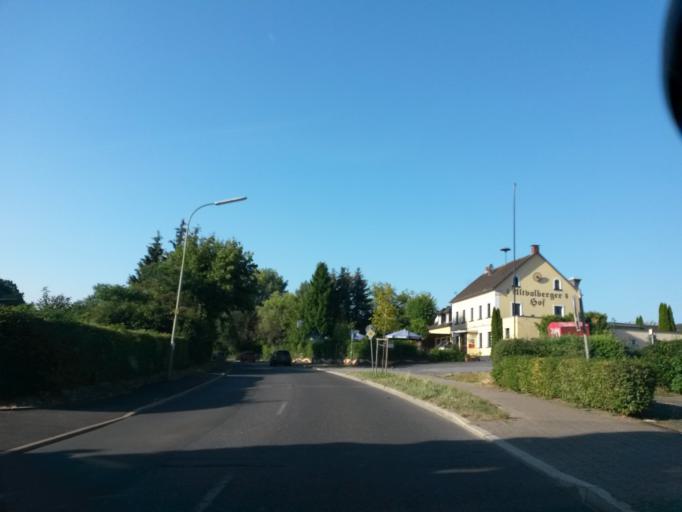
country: DE
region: North Rhine-Westphalia
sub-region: Regierungsbezirk Koln
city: Rosrath
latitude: 50.9154
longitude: 7.1739
